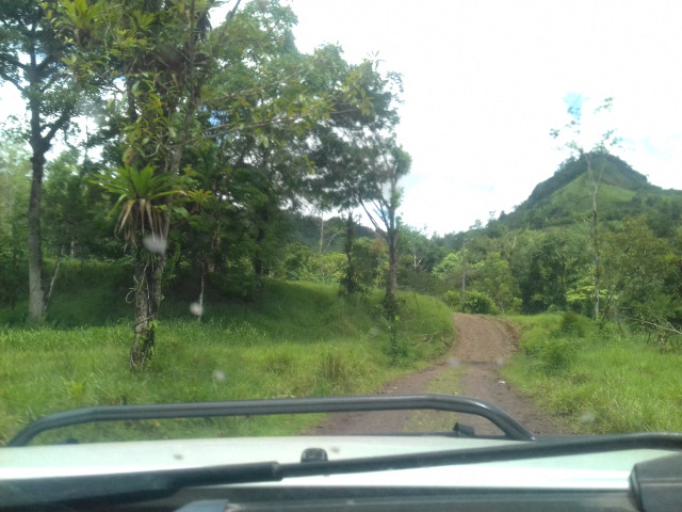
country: NI
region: Matagalpa
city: Rio Blanco
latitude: 13.0321
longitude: -85.2303
